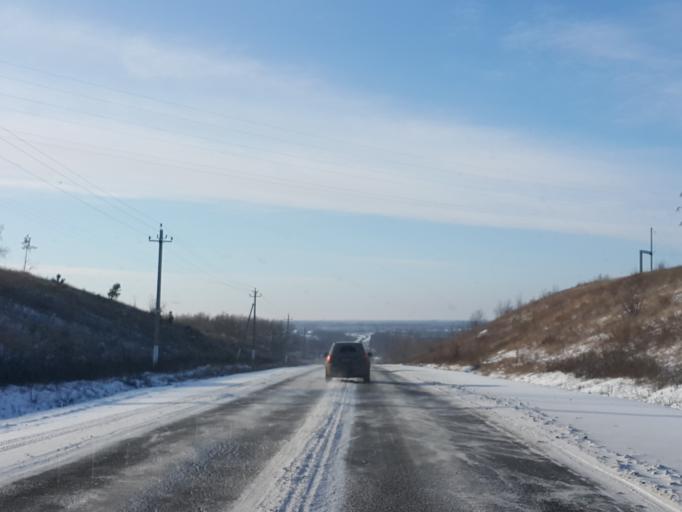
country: RU
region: Tambov
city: Znamenka
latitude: 52.4185
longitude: 41.4903
